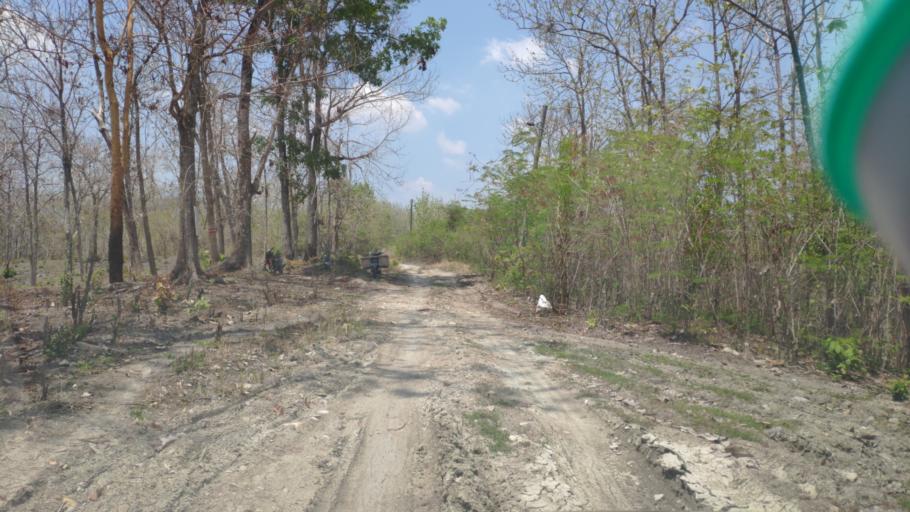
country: ID
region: Central Java
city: Randublatung
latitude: -7.2673
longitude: 111.3317
